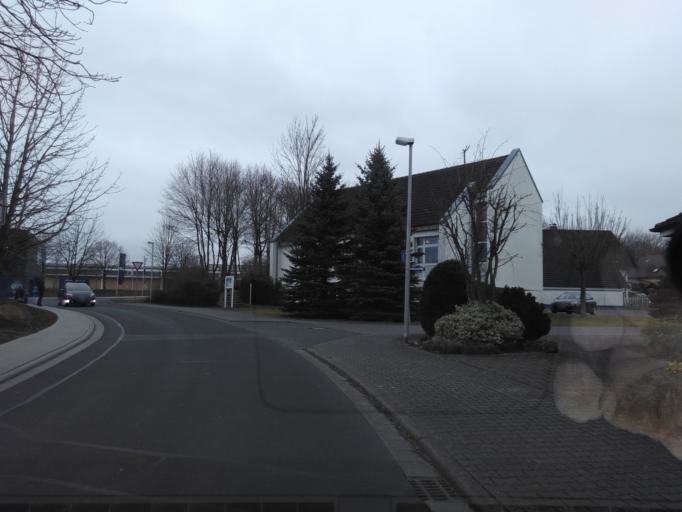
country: DE
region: Rheinland-Pfalz
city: Montabaur
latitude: 50.4281
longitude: 7.8172
